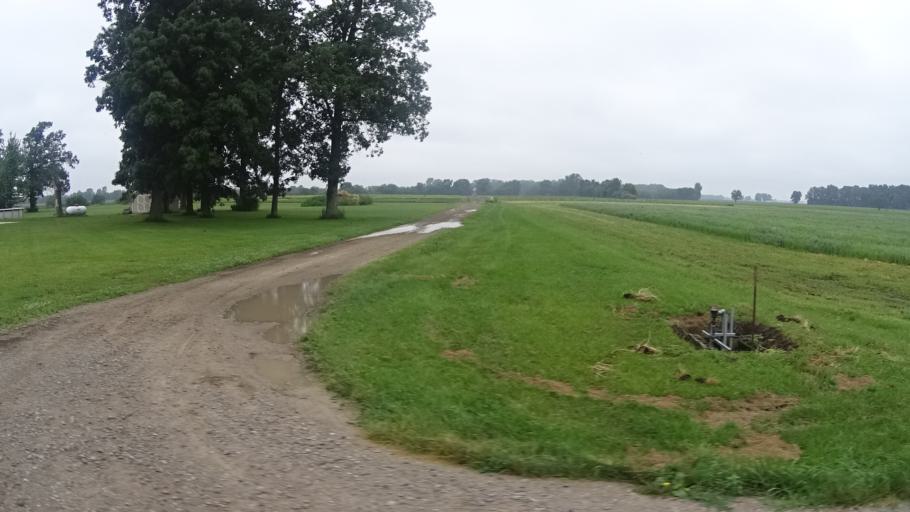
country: US
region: Ohio
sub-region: Erie County
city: Milan
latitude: 41.3588
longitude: -82.6242
